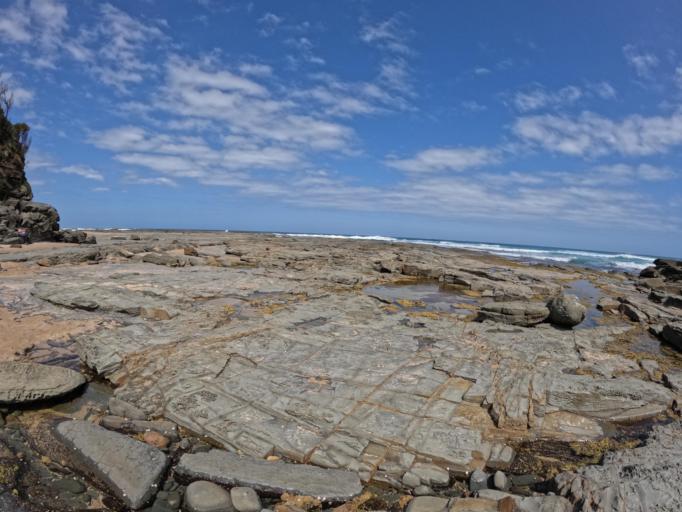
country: AU
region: Victoria
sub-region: Colac-Otway
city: Apollo Bay
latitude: -38.7926
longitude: 143.6234
